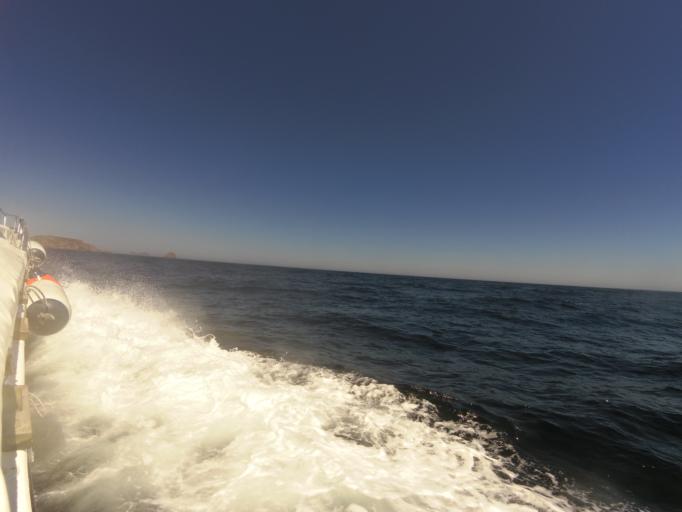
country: PT
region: Leiria
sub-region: Peniche
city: Peniche
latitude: 39.3978
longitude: -9.4836
